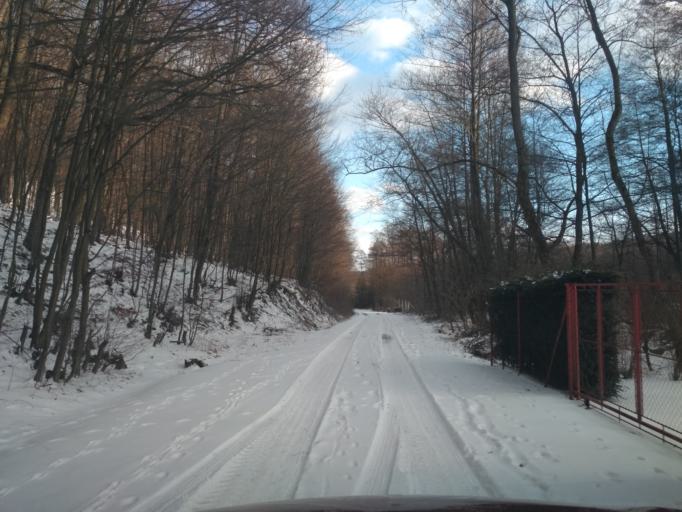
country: SK
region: Kosicky
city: Kosice
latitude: 48.7389
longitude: 21.1554
